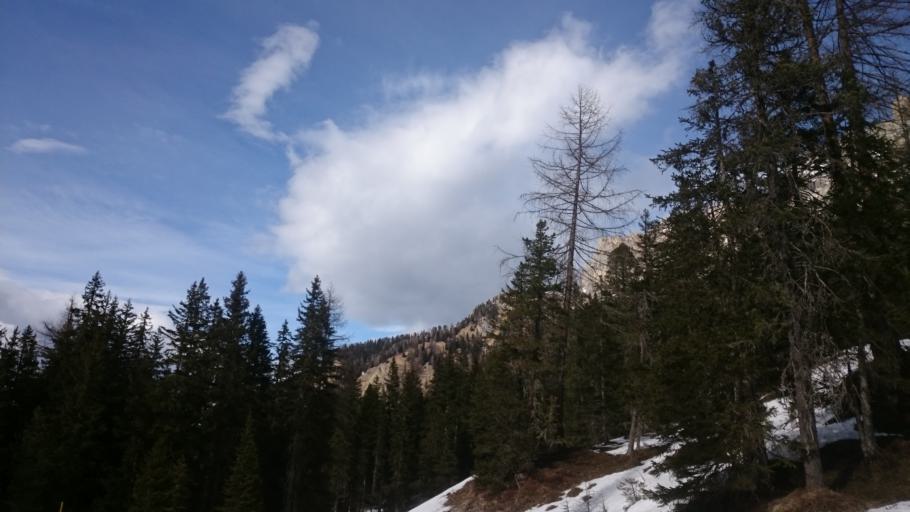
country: IT
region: Trentino-Alto Adige
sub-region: Bolzano
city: Braies
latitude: 46.6618
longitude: 12.1650
